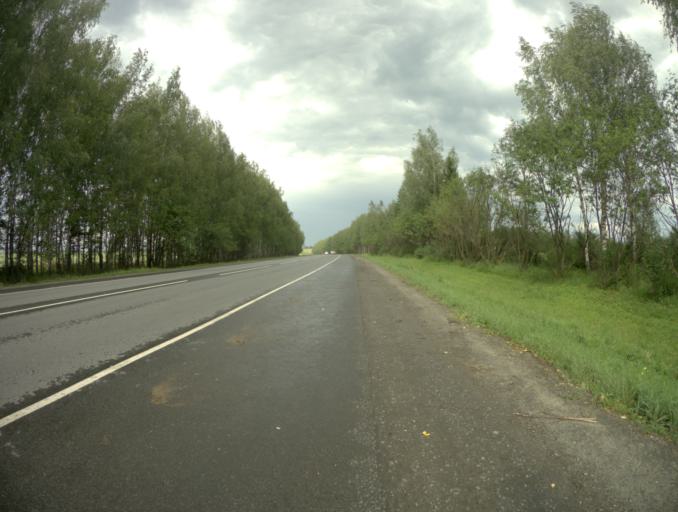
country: RU
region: Vladimir
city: Bogolyubovo
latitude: 56.2593
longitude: 40.4634
